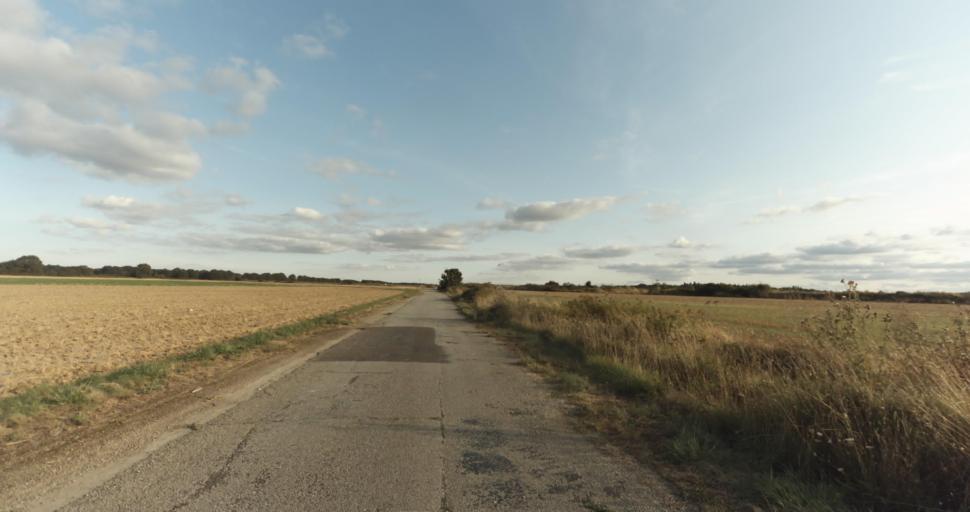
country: FR
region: Haute-Normandie
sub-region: Departement de l'Eure
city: Marcilly-sur-Eure
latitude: 48.8907
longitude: 1.2730
